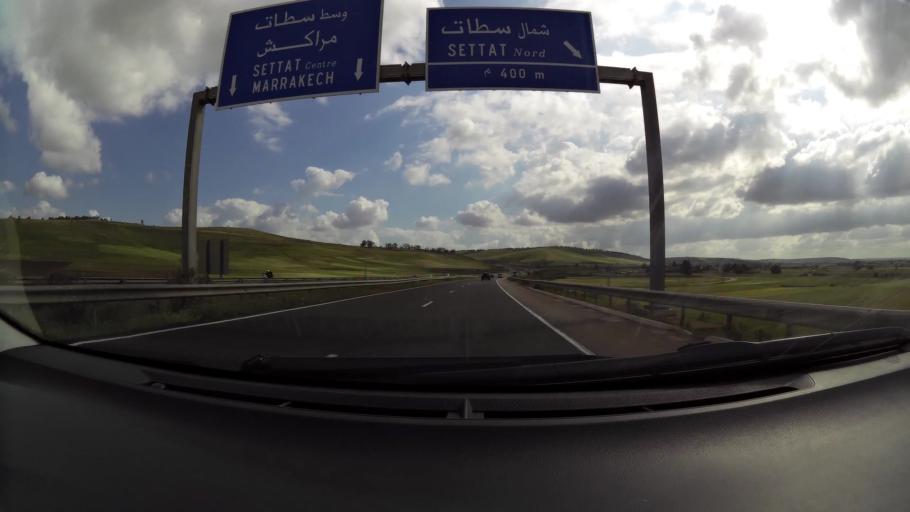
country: MA
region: Chaouia-Ouardigha
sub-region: Settat Province
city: Settat
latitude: 33.0810
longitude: -7.5914
